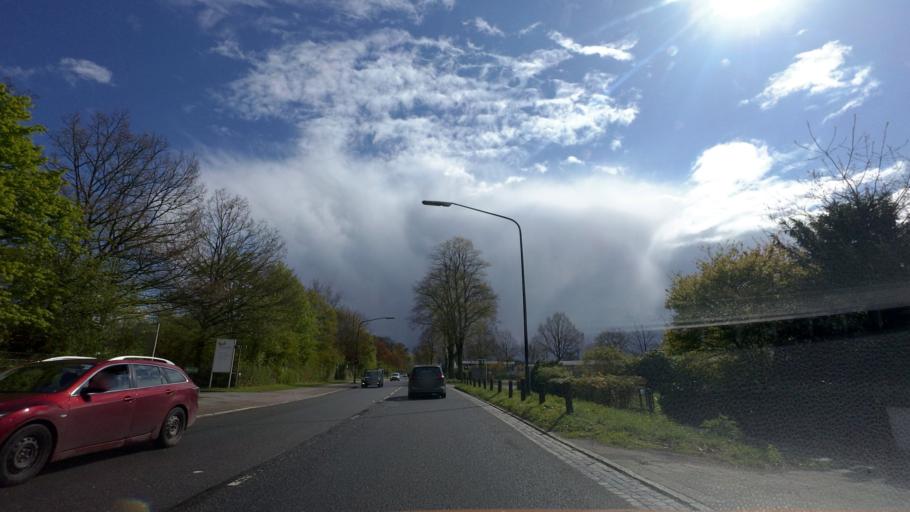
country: DE
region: Lower Saxony
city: Oyten
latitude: 53.0575
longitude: 8.9561
